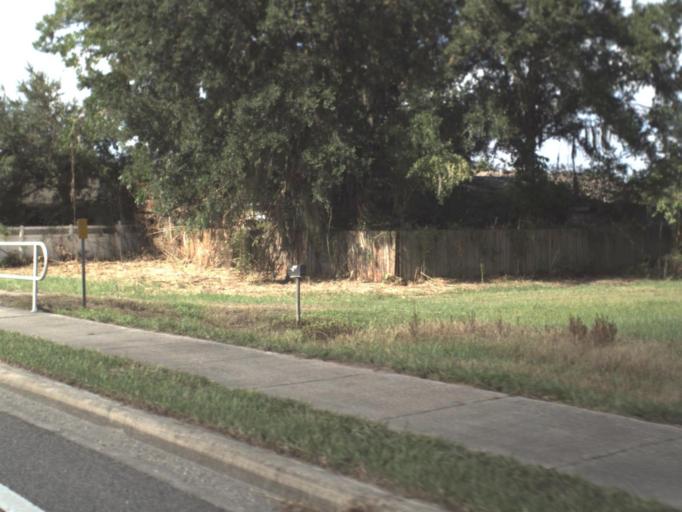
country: US
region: Florida
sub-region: Pasco County
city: Land O' Lakes
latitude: 28.2434
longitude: -82.4609
